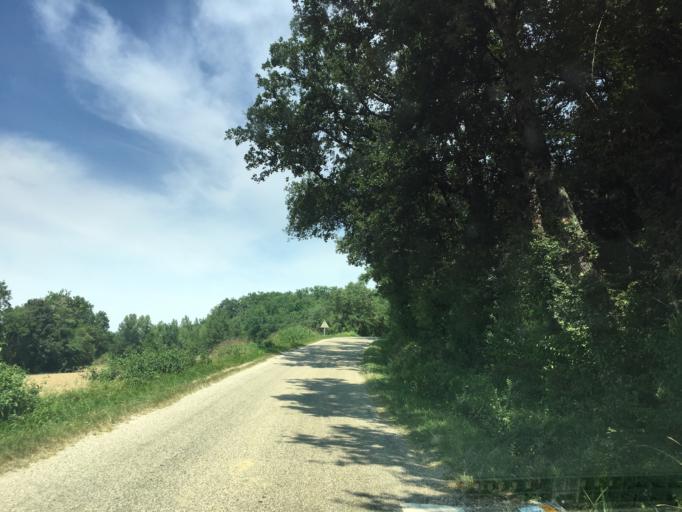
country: FR
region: Midi-Pyrenees
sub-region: Departement du Gers
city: Jegun
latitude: 43.7911
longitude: 0.4871
